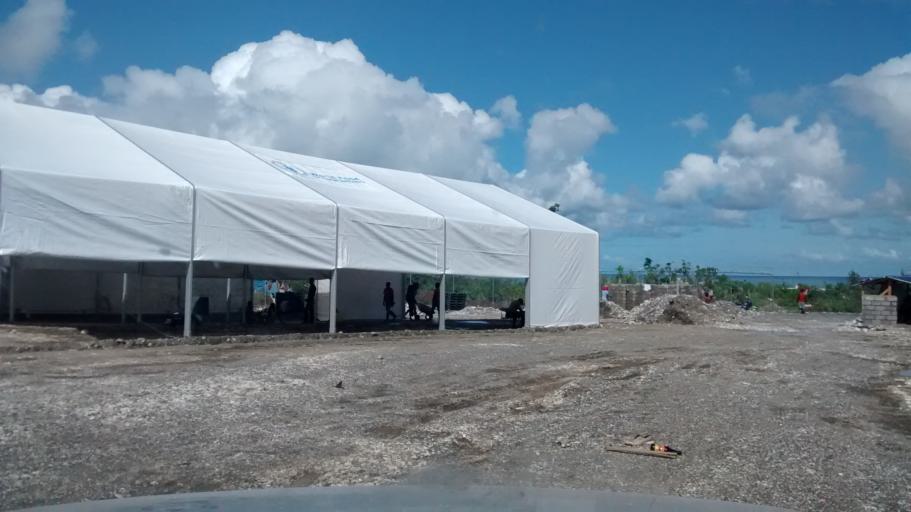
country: HT
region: Grandans
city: Jeremie
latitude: 18.6219
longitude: -74.0913
